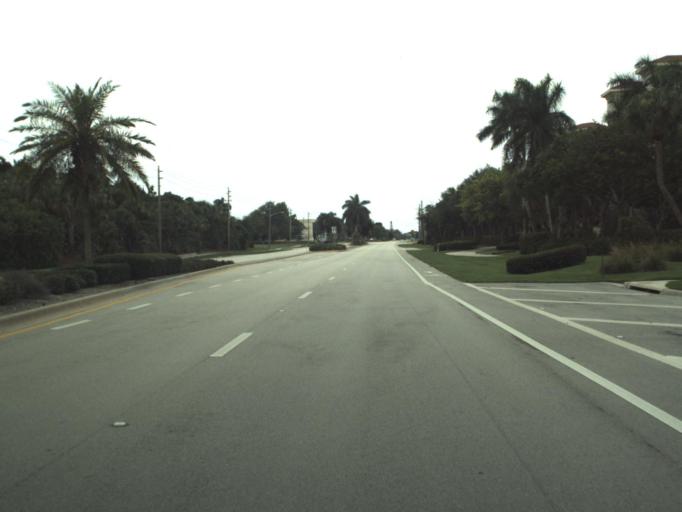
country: US
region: Florida
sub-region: Palm Beach County
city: Jupiter
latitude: 26.9296
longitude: -80.0786
